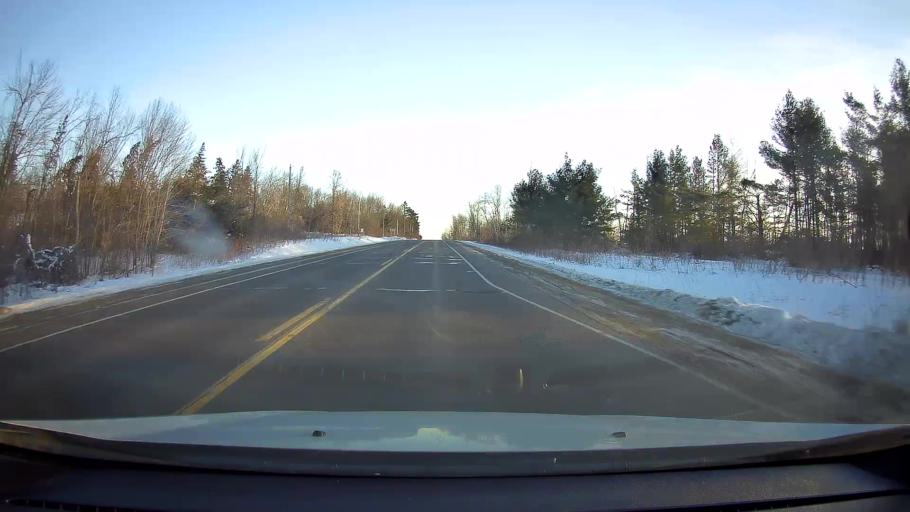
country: US
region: Wisconsin
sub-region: Barron County
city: Turtle Lake
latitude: 45.4672
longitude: -92.0902
